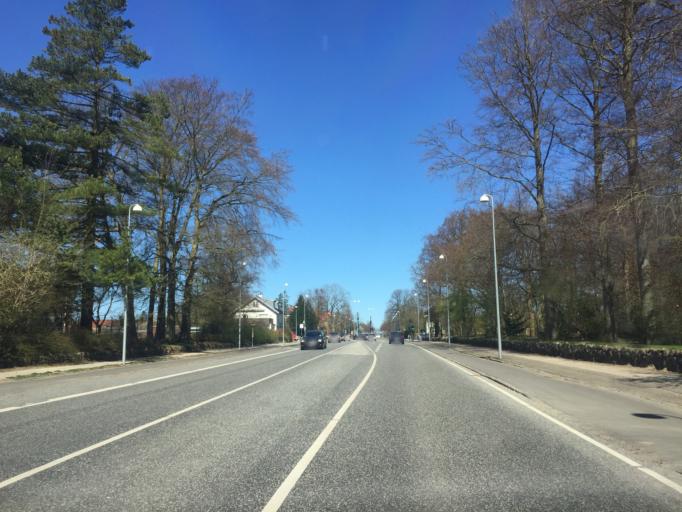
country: DK
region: Capital Region
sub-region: Lyngby-Tarbaek Kommune
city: Kongens Lyngby
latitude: 55.7825
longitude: 12.4916
